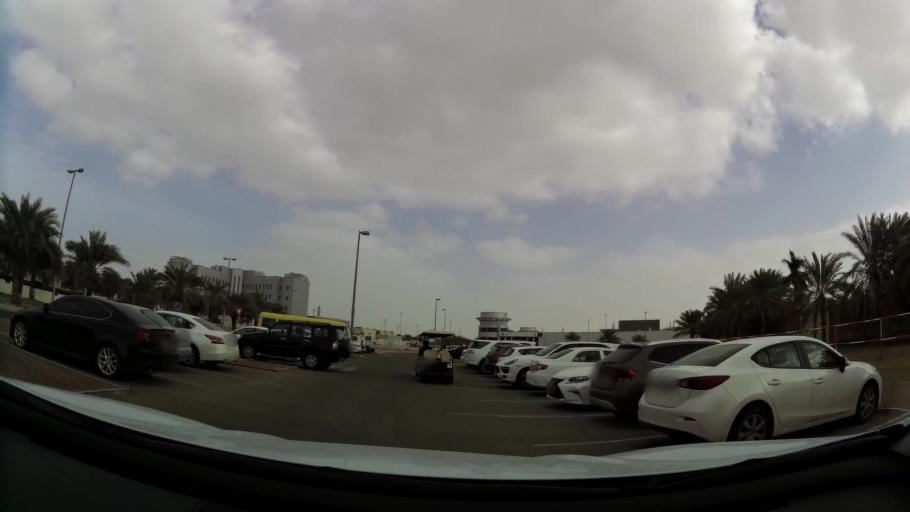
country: AE
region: Abu Dhabi
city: Abu Dhabi
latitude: 24.4154
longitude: 54.4928
